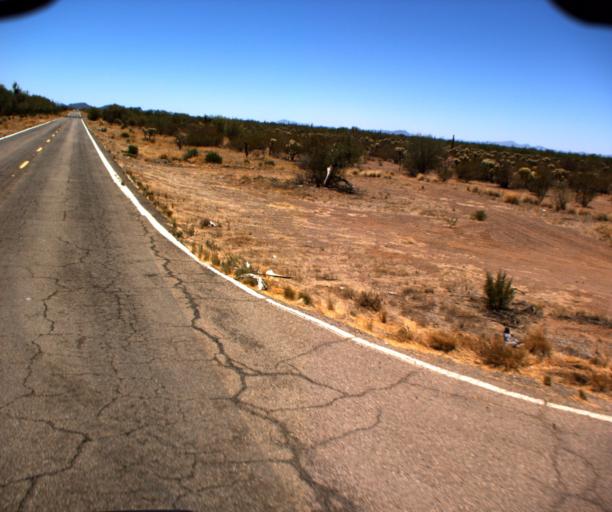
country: US
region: Arizona
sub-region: Pima County
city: Sells
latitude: 32.0563
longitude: -112.0304
